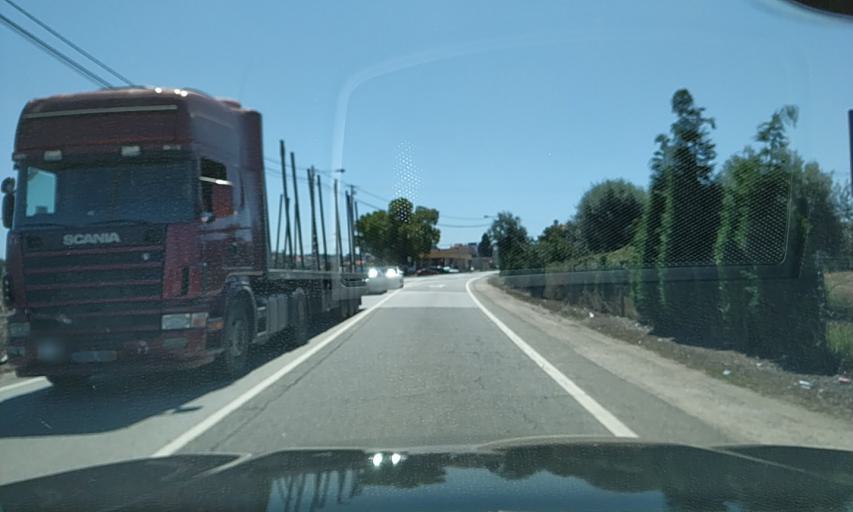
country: PT
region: Aveiro
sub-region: Anadia
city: Arcos
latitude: 40.4568
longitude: -8.4545
